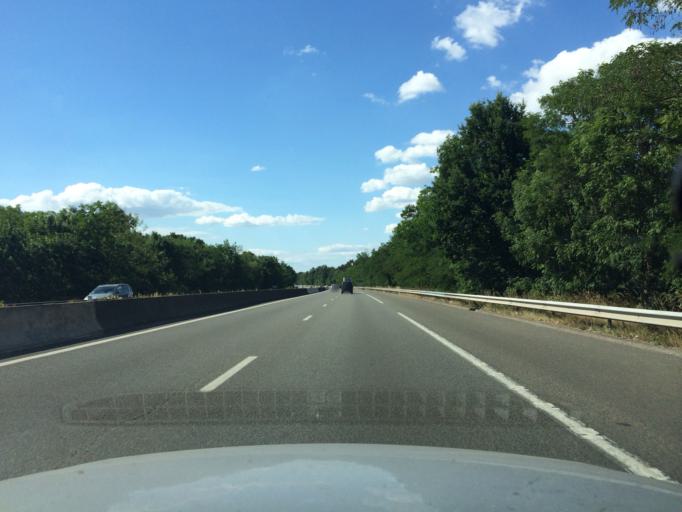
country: FR
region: Alsace
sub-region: Departement du Bas-Rhin
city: Vendenheim
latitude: 48.6902
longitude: 7.7273
